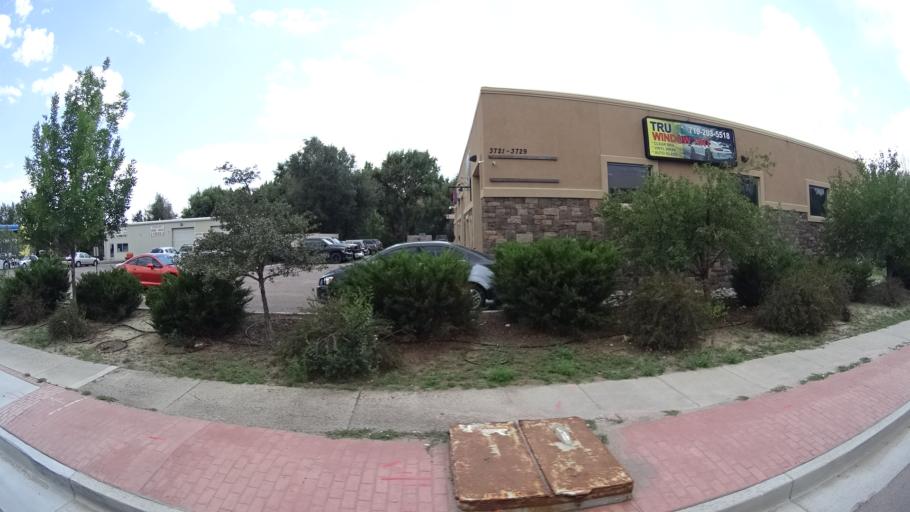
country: US
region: Colorado
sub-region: El Paso County
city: Colorado Springs
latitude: 38.8319
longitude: -104.7609
